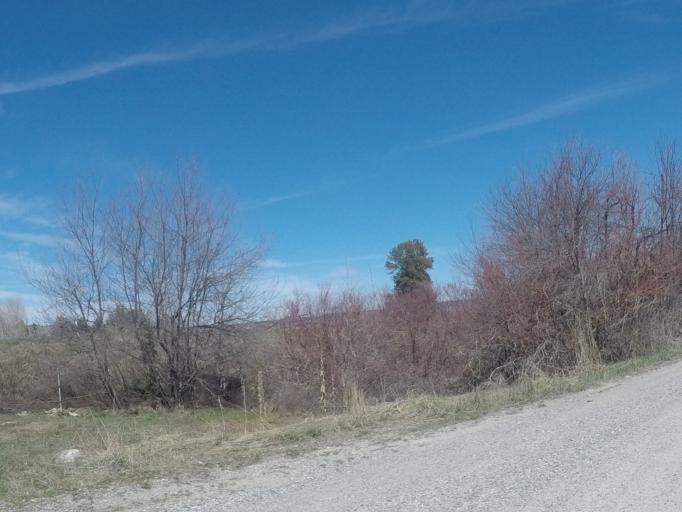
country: US
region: Montana
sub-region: Stillwater County
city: Columbus
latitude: 45.6237
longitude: -109.2898
